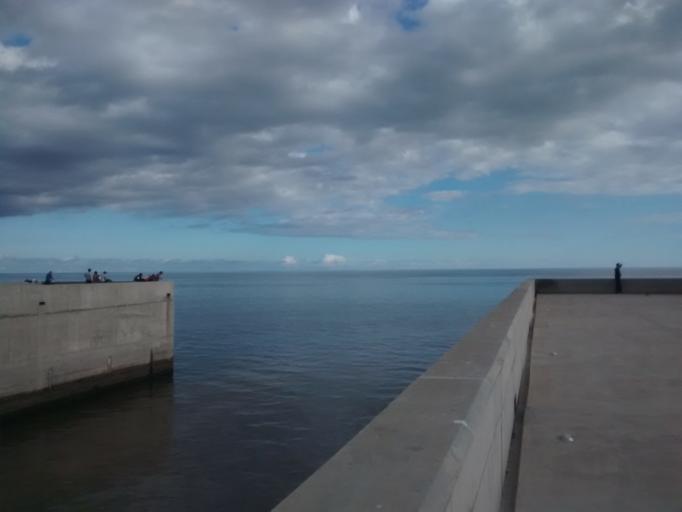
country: PT
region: Madeira
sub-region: Funchal
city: Funchal
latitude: 32.6465
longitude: -16.9050
